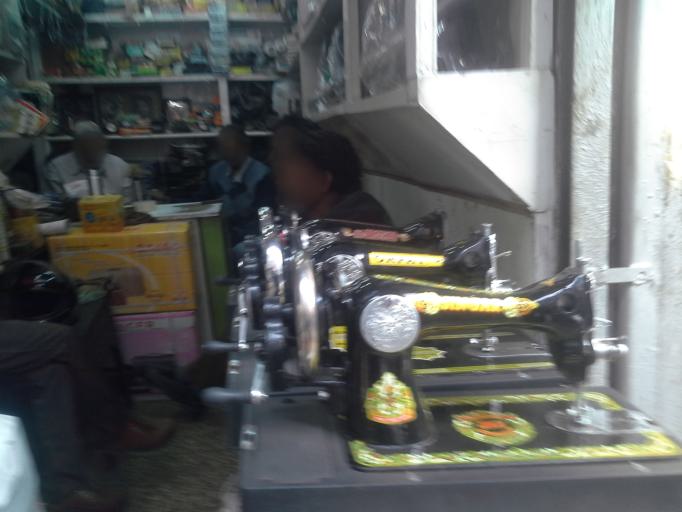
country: IN
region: NCT
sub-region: North Delhi
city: Delhi
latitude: 28.6538
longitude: 77.2283
